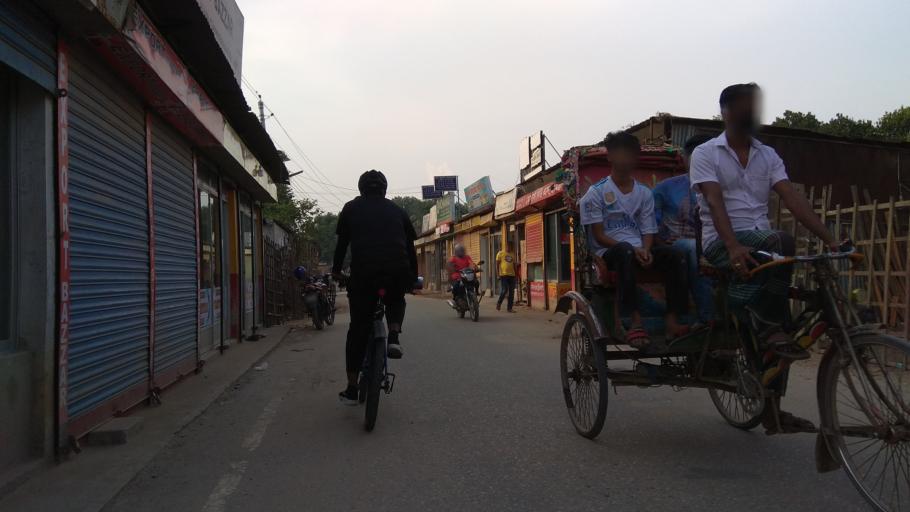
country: BD
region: Dhaka
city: Tungi
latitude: 23.8330
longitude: 90.3889
